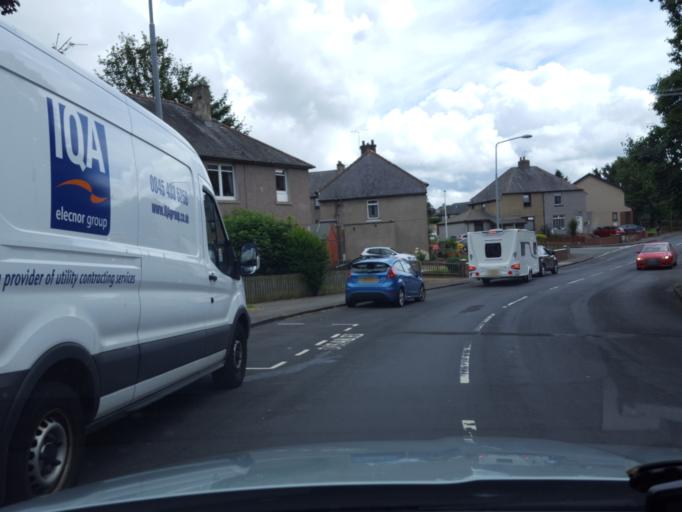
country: GB
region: Scotland
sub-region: West Lothian
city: Bathgate
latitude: 55.9067
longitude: -3.6480
